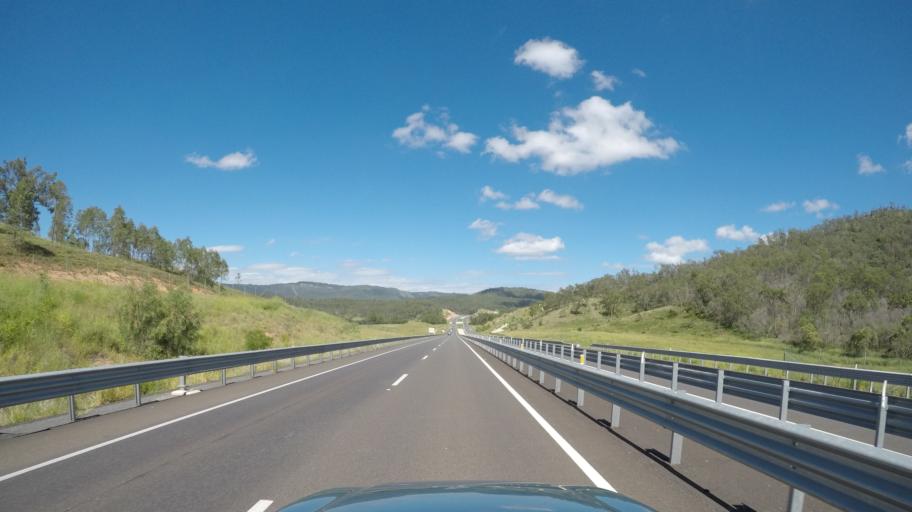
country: AU
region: Queensland
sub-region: Toowoomba
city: East Toowoomba
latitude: -27.5149
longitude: 152.0375
